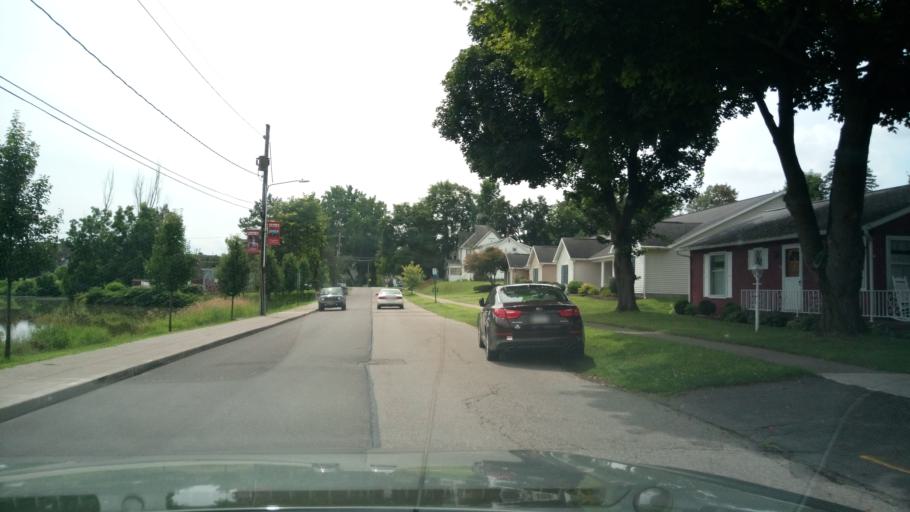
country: US
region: Pennsylvania
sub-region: Bradford County
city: Sayre
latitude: 41.9844
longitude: -76.5219
